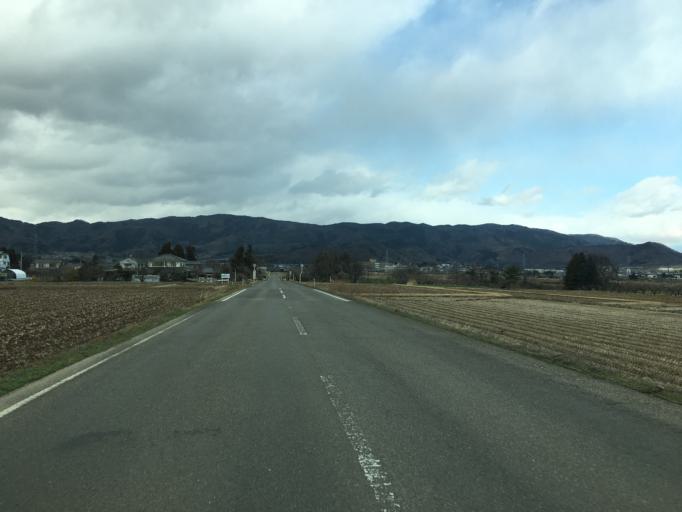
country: JP
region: Fukushima
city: Hobaramachi
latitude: 37.8598
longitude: 140.5381
